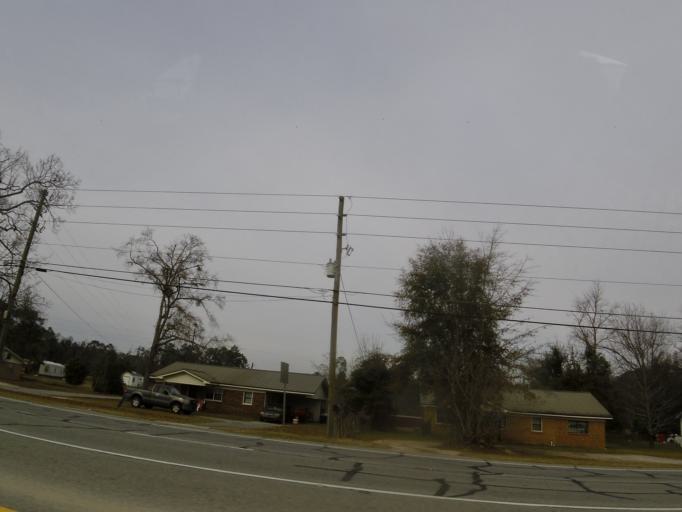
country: US
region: Georgia
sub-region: Decatur County
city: Bainbridge
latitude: 30.9289
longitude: -84.6273
